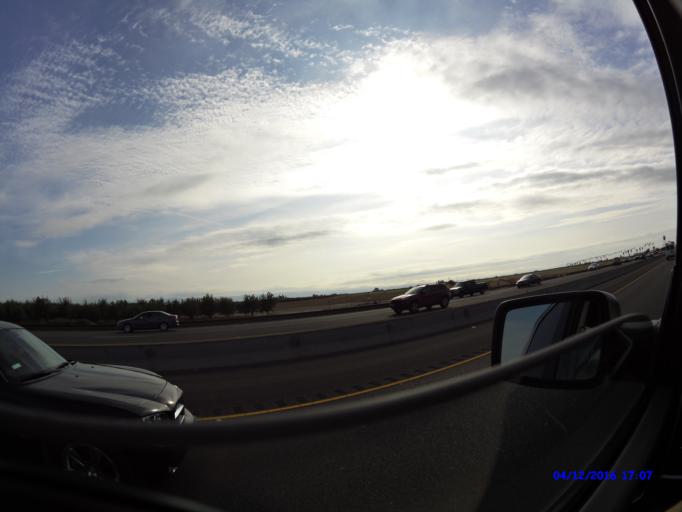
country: US
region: California
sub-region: San Joaquin County
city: Ripon
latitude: 37.7597
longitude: -121.1552
